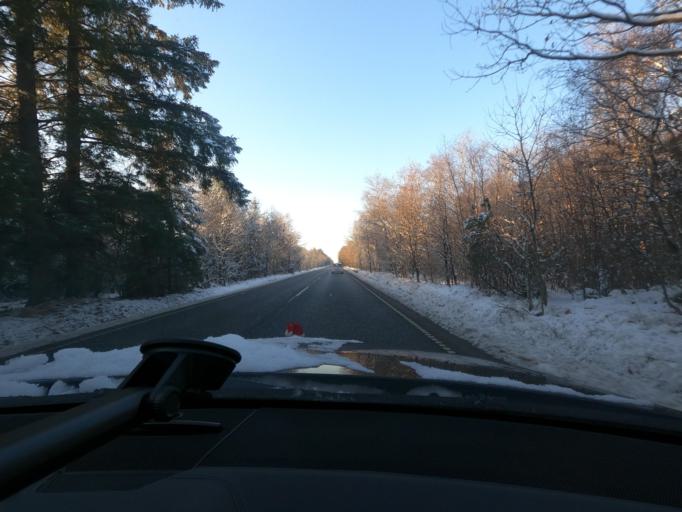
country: DK
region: South Denmark
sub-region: Tonder Kommune
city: Sherrebek
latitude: 55.1745
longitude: 8.8575
